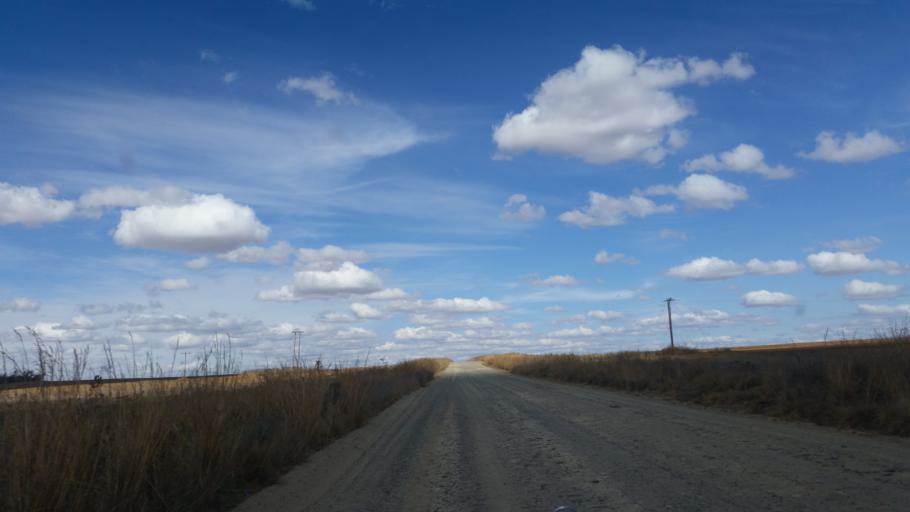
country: ZA
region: Orange Free State
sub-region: Thabo Mofutsanyana District Municipality
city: Bethlehem
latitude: -28.1513
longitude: 28.6550
